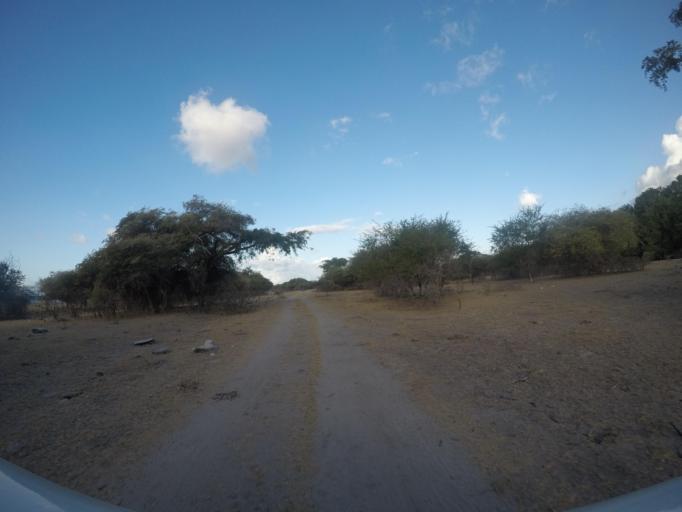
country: TL
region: Lautem
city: Lospalos
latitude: -8.3248
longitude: 126.9875
